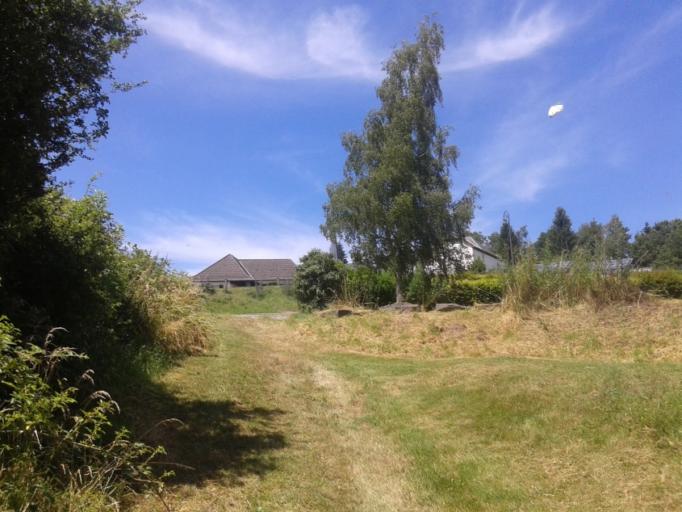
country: LU
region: Diekirch
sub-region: Canton de Diekirch
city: Bourscheid
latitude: 49.9312
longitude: 6.0644
